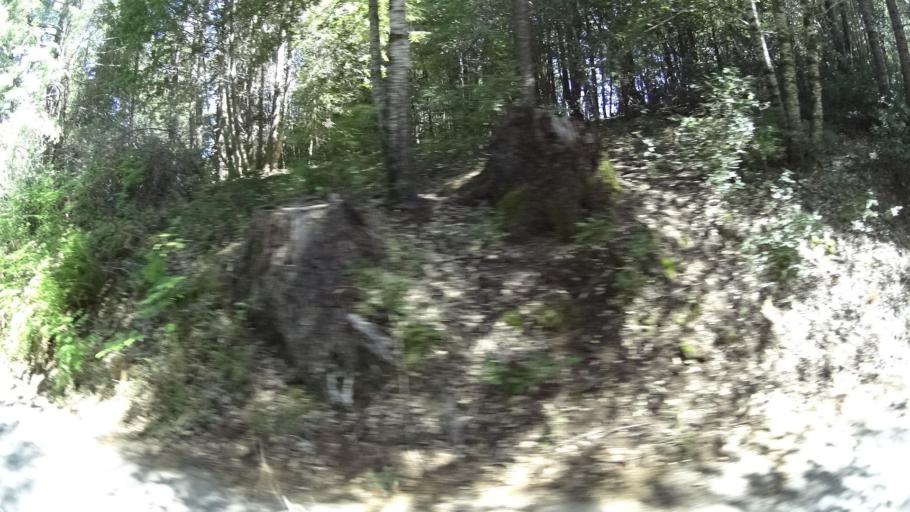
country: US
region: California
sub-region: Humboldt County
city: Redway
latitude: 40.1520
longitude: -124.0366
